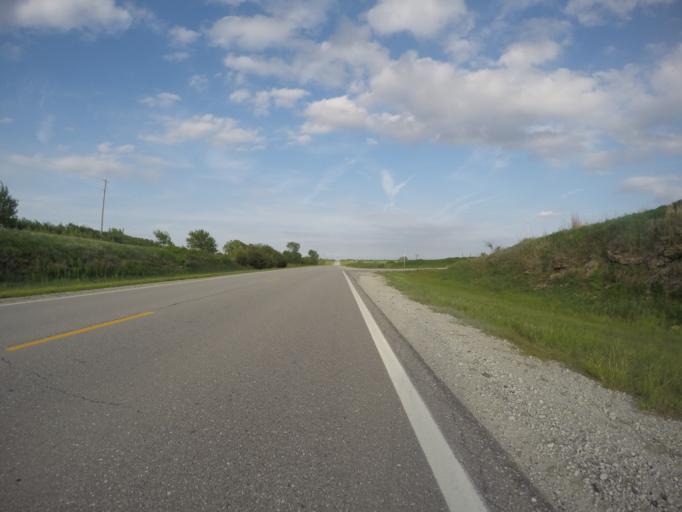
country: US
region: Kansas
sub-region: Pottawatomie County
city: Westmoreland
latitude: 39.4282
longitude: -96.5813
